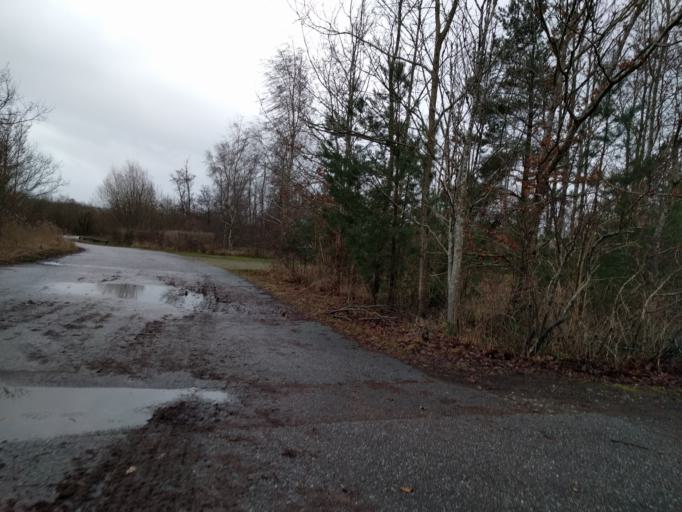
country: DK
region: Central Jutland
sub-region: Randers Kommune
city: Randers
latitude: 56.4615
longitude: 10.0190
